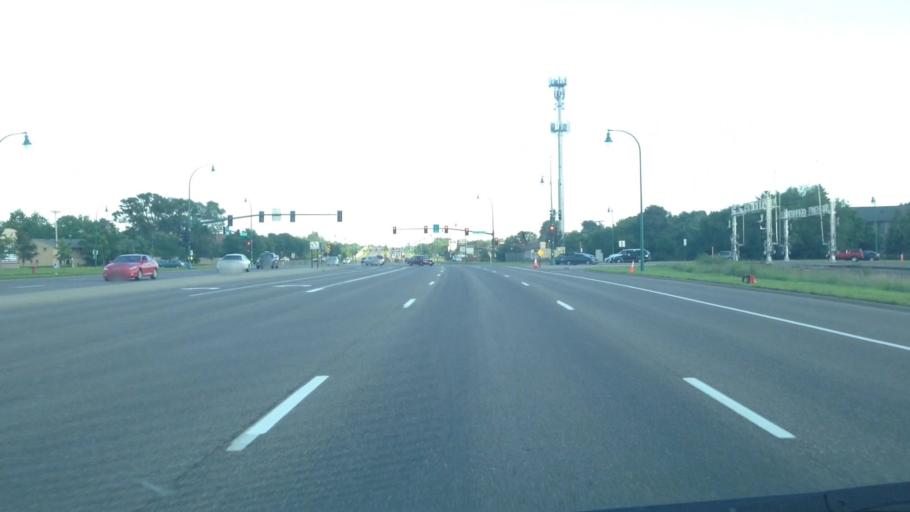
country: US
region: Minnesota
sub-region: Hennepin County
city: Crystal
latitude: 45.0557
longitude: -93.3592
